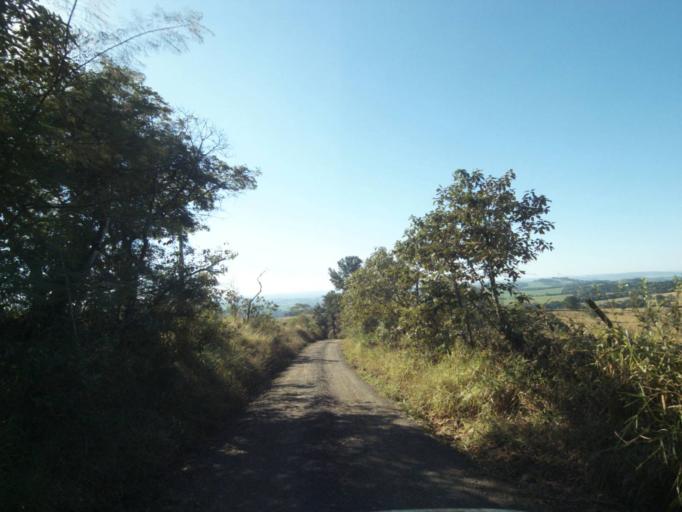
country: BR
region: Parana
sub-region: Tibagi
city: Tibagi
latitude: -24.5404
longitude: -50.4683
